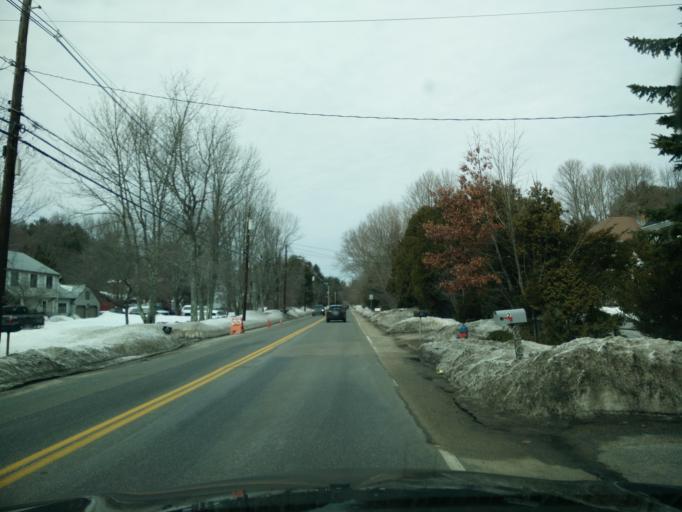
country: US
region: Massachusetts
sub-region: Norfolk County
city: Walpole
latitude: 42.1718
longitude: -71.2408
